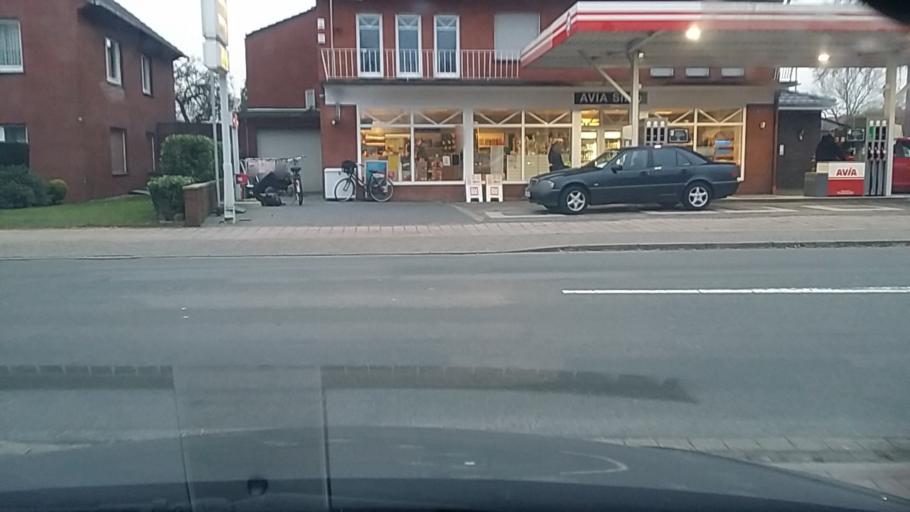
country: DE
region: Lower Saxony
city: Twist
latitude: 52.6343
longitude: 7.0589
